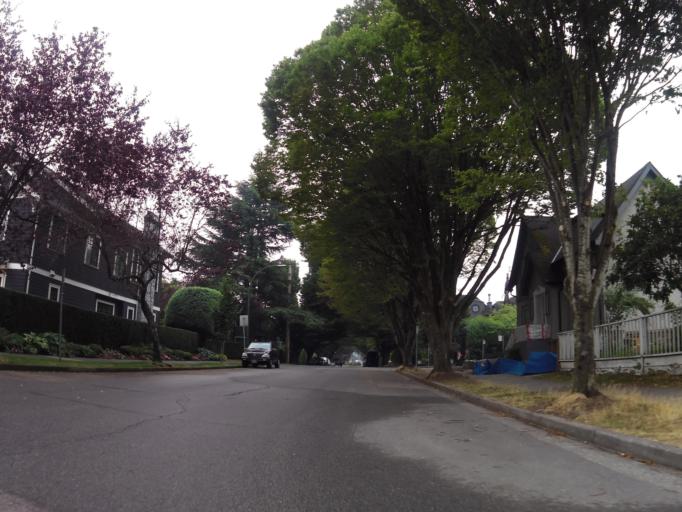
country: CA
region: British Columbia
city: West End
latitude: 49.2758
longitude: -123.1478
